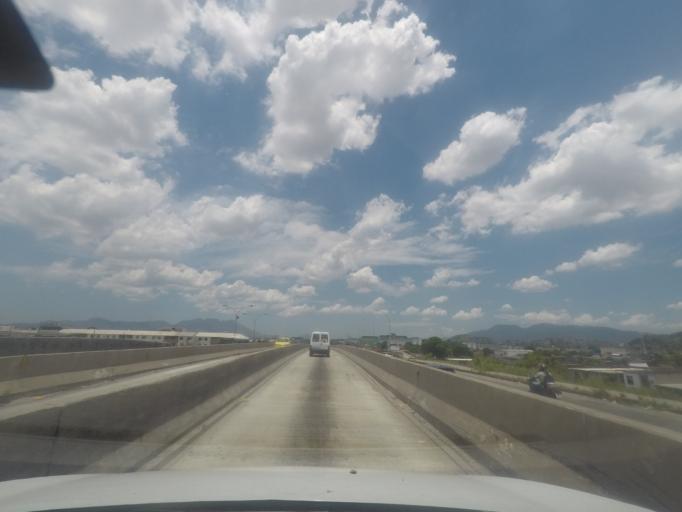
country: BR
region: Rio de Janeiro
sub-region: Sao Joao De Meriti
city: Sao Joao de Meriti
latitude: -22.8291
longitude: -43.3456
